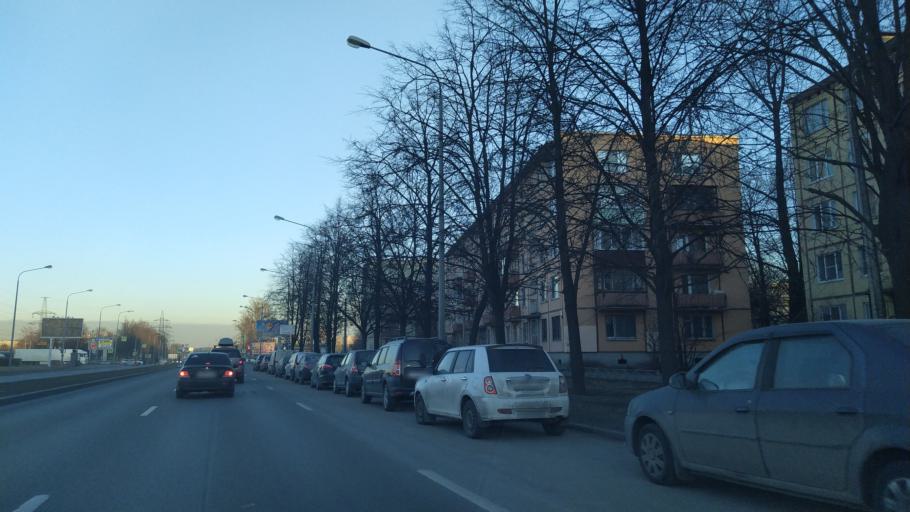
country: RU
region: Leningrad
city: Kalininskiy
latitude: 59.9769
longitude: 30.3990
